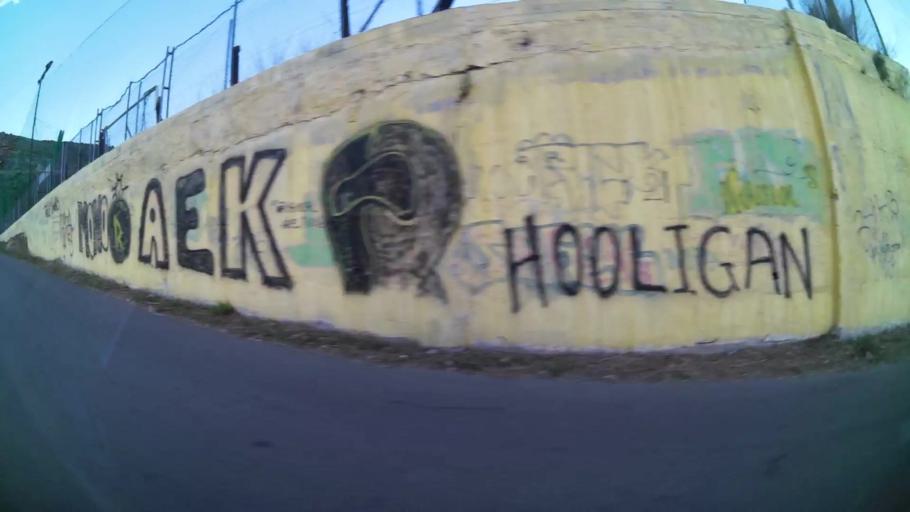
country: GR
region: Attica
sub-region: Nomarchia Dytikis Attikis
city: Ano Liosia
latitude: 38.0957
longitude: 23.6999
